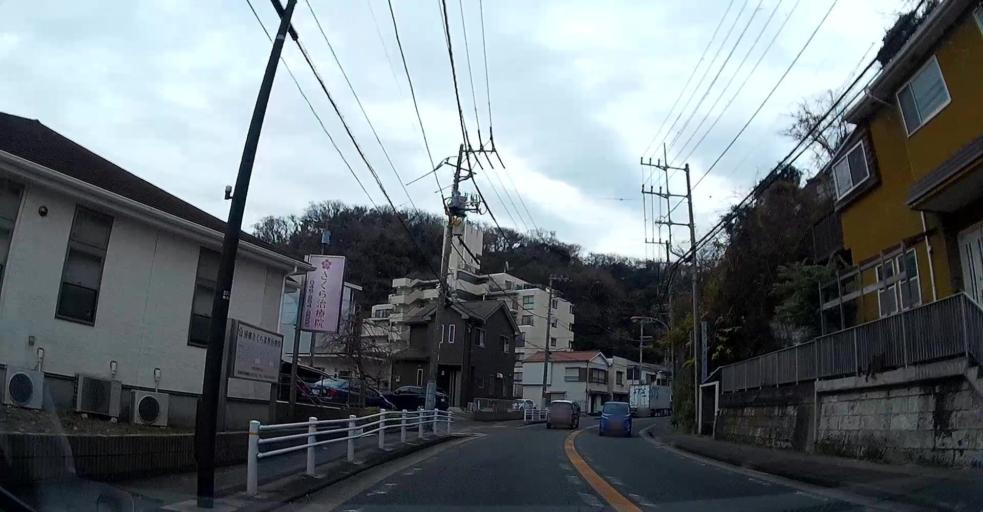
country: JP
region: Kanagawa
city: Yokosuka
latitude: 35.3075
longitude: 139.6369
